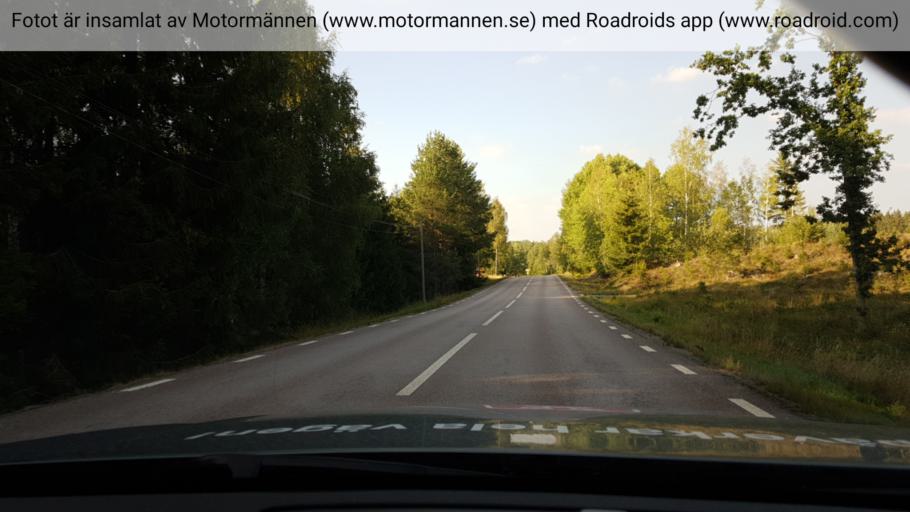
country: SE
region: Soedermanland
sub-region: Strangnas Kommun
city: Mariefred
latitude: 59.1998
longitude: 17.1910
